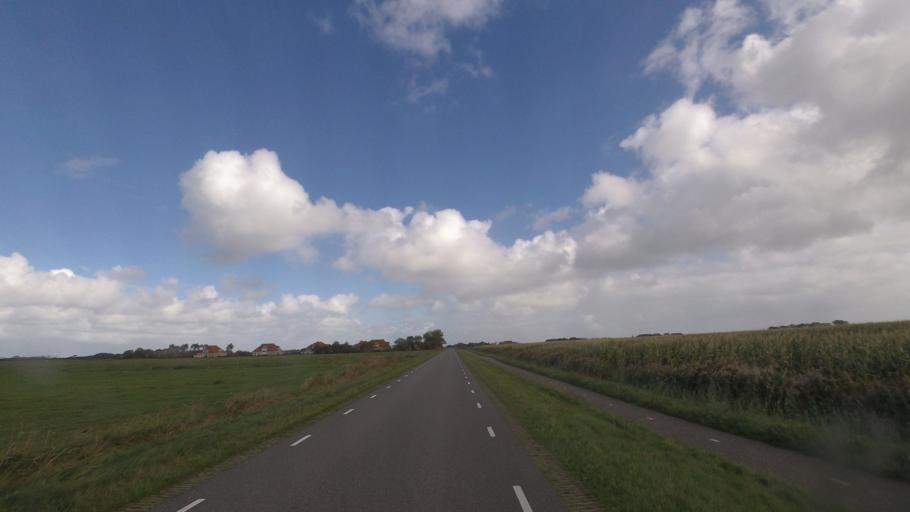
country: NL
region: Friesland
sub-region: Gemeente Ameland
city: Hollum
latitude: 53.4375
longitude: 5.6508
